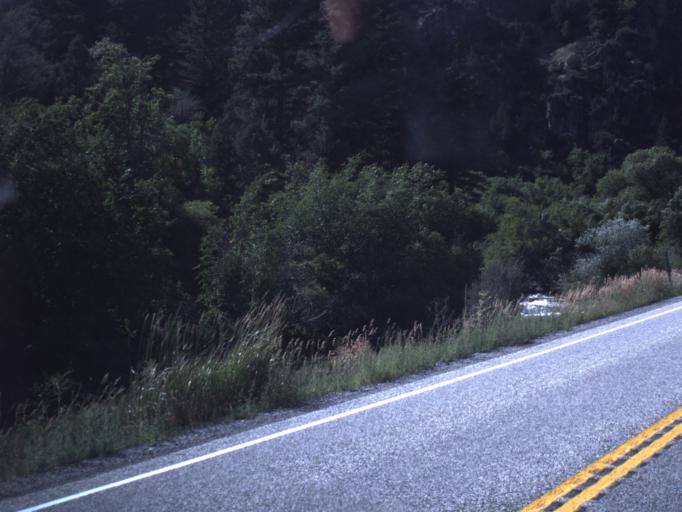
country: US
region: Utah
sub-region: Cache County
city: North Logan
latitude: 41.7883
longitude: -111.6451
